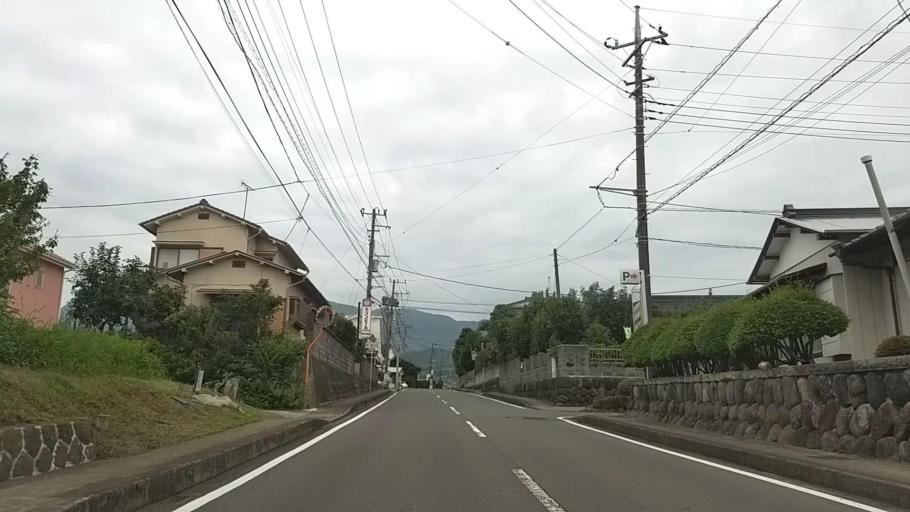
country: JP
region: Kanagawa
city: Odawara
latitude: 35.3273
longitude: 139.0892
